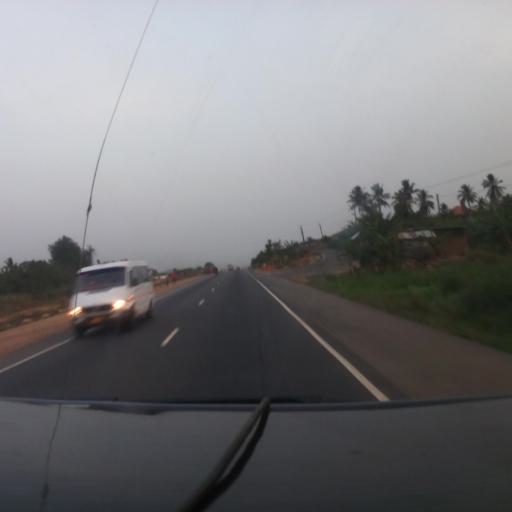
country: GH
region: Eastern
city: Nsawam
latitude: 5.8798
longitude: -0.3740
